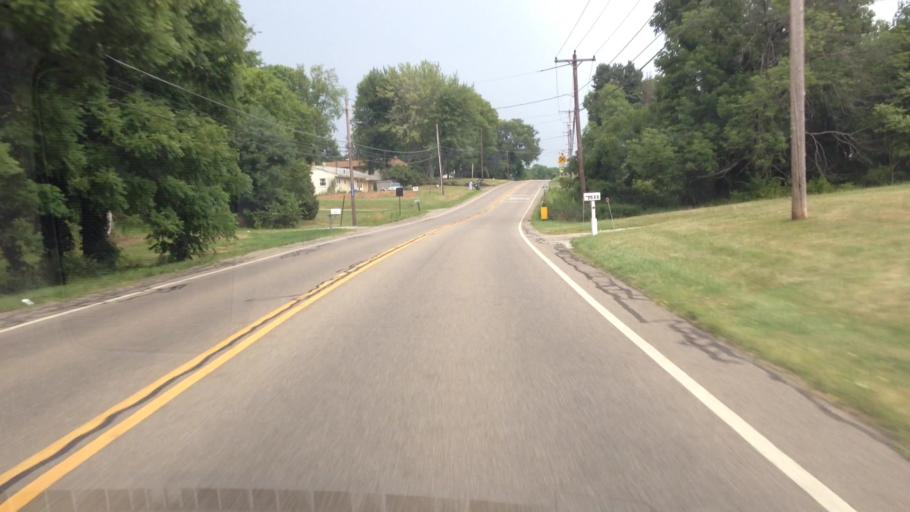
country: US
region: Ohio
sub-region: Stark County
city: Uniontown
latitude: 40.9764
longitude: -81.4307
